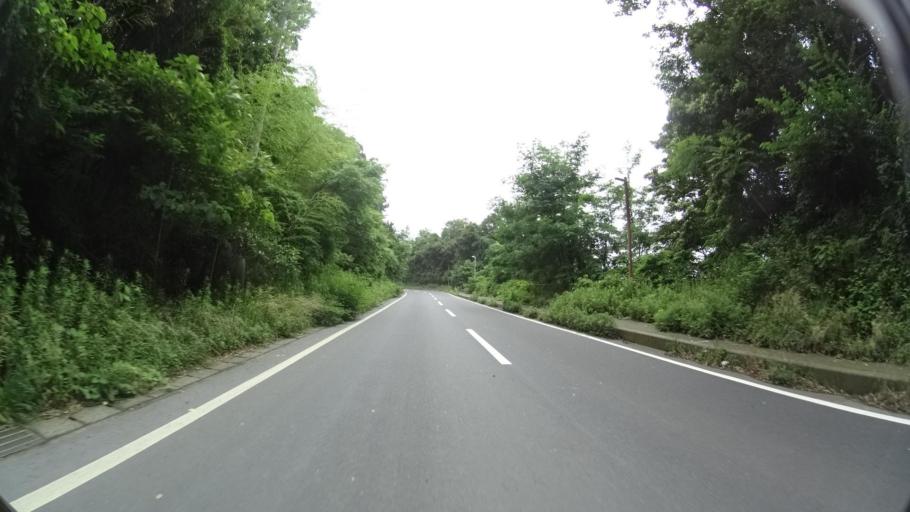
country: JP
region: Kyoto
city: Maizuru
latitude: 35.5016
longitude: 135.3850
